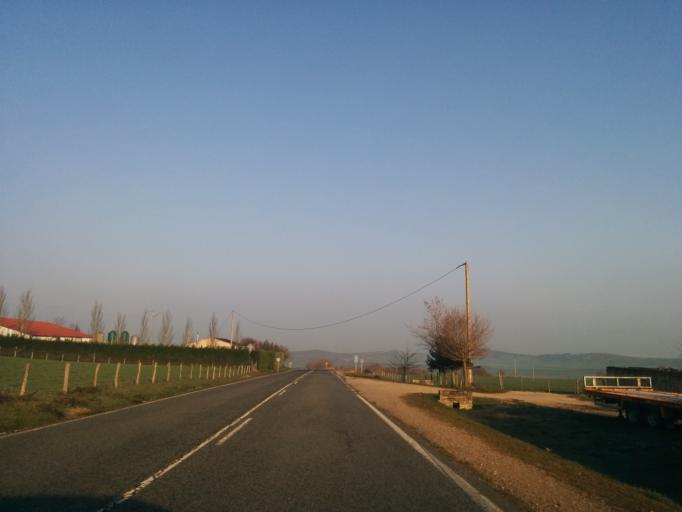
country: ES
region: Navarre
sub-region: Provincia de Navarra
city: Elorz
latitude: 42.7571
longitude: -1.5519
